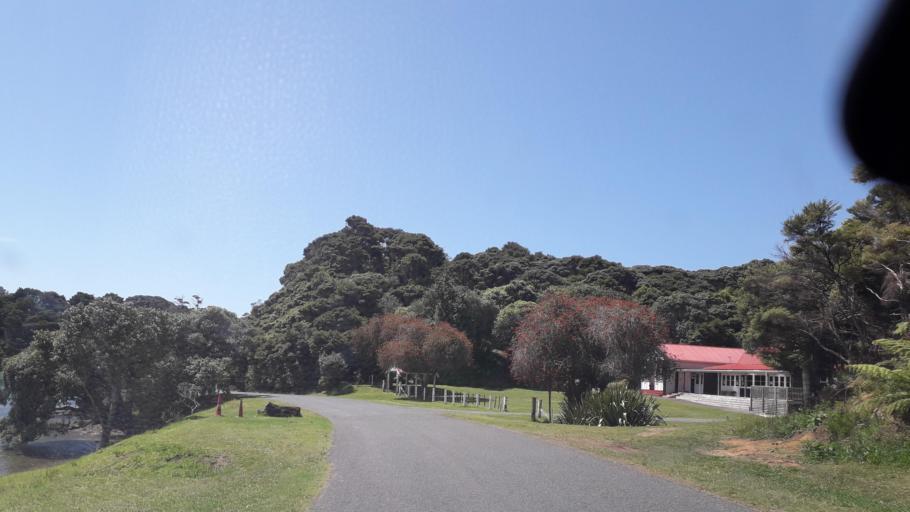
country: NZ
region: Northland
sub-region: Far North District
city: Paihia
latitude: -35.2340
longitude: 174.2607
